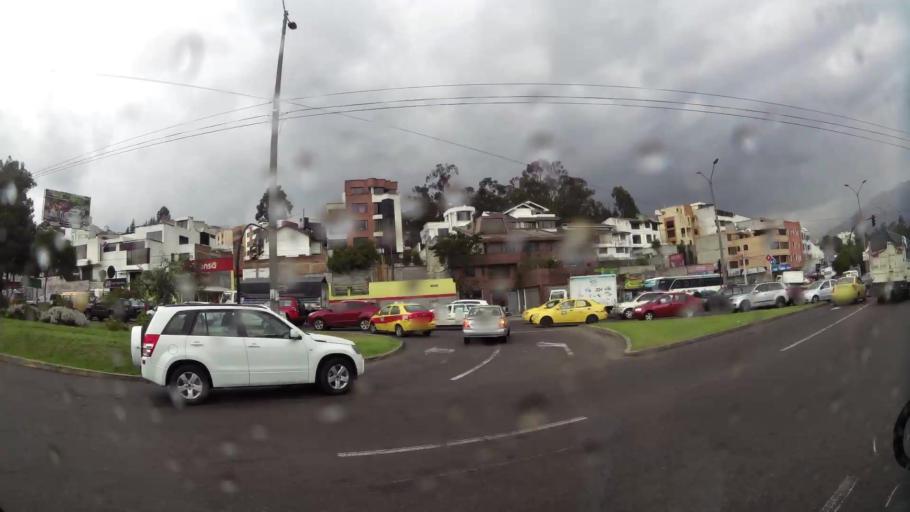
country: EC
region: Pichincha
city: Quito
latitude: -0.0943
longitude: -78.4819
